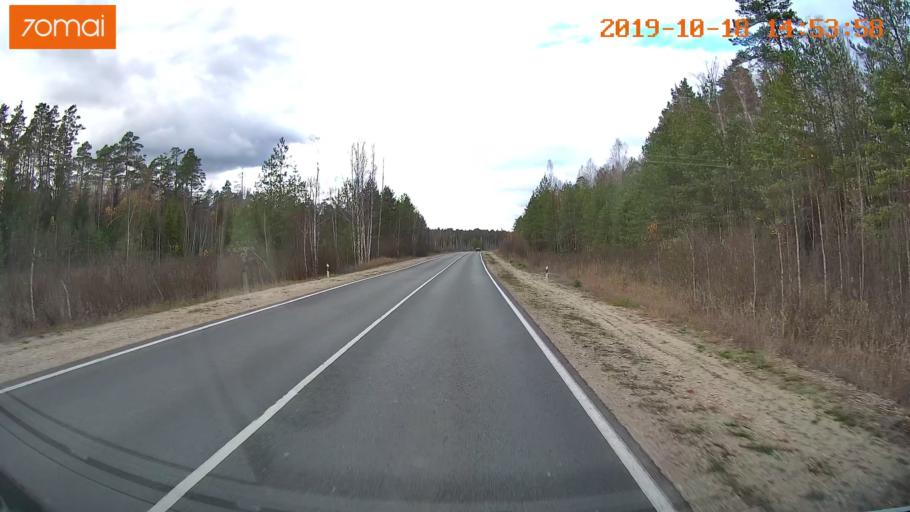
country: RU
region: Vladimir
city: Kurlovo
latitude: 55.4354
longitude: 40.6070
